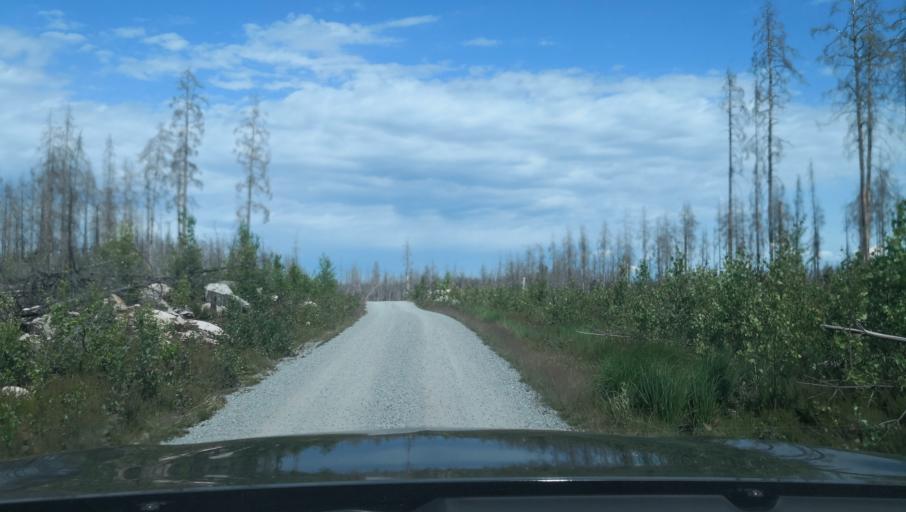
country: SE
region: Vaestmanland
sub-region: Surahammars Kommun
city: Ramnas
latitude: 59.9198
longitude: 16.1614
